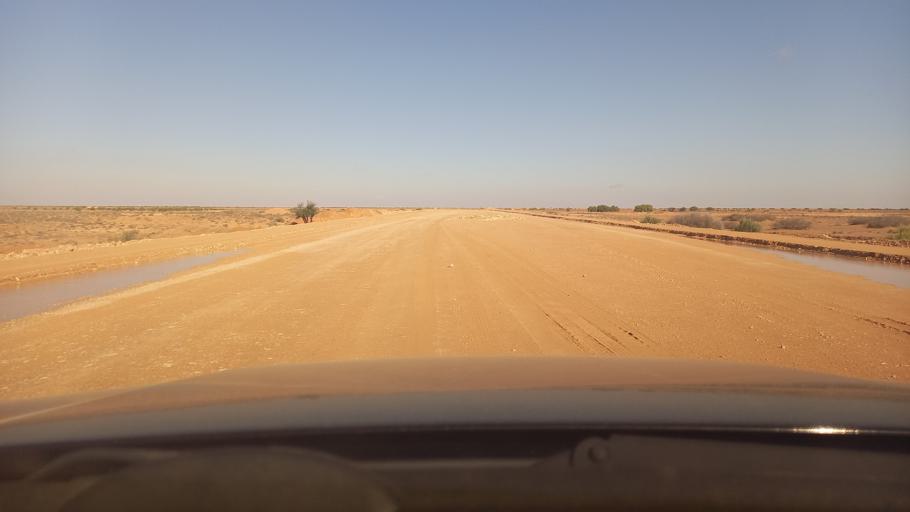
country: TN
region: Tataouine
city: Tataouine
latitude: 33.1387
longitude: 10.5053
